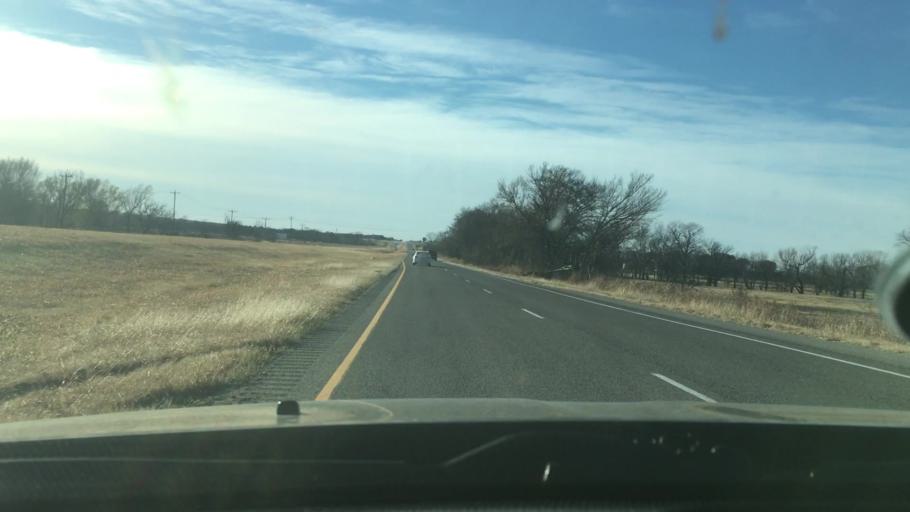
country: US
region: Oklahoma
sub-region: Murray County
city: Davis
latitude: 34.5066
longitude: -97.1509
